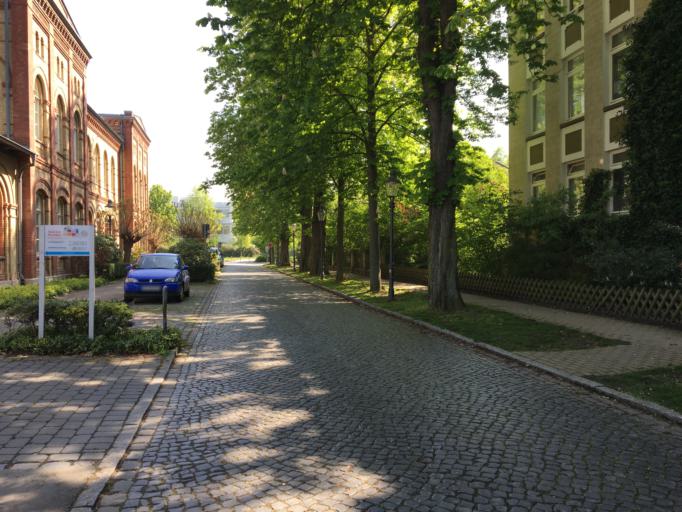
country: DE
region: Lower Saxony
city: Braunschweig
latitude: 52.2778
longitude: 10.5274
